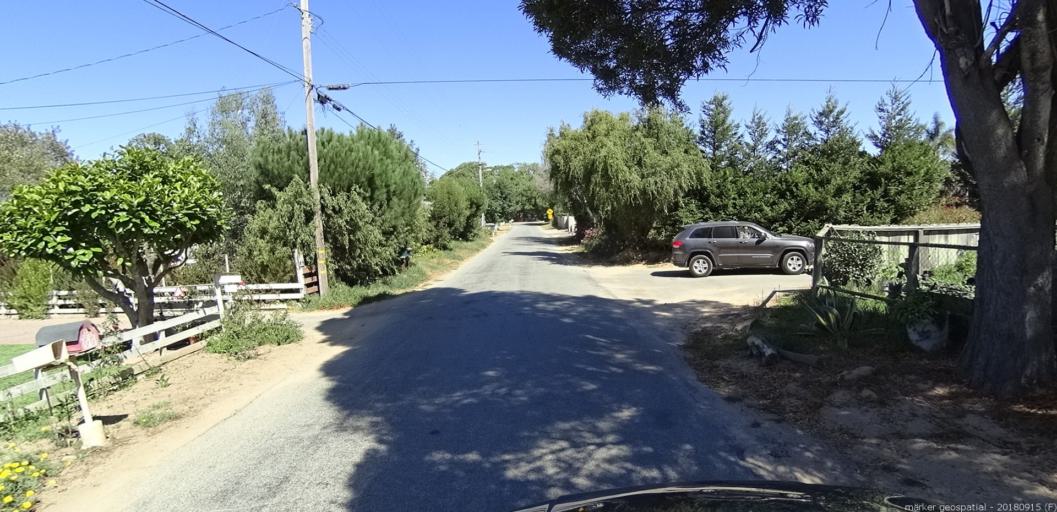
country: US
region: California
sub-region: Monterey County
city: Las Lomas
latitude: 36.8557
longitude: -121.7040
